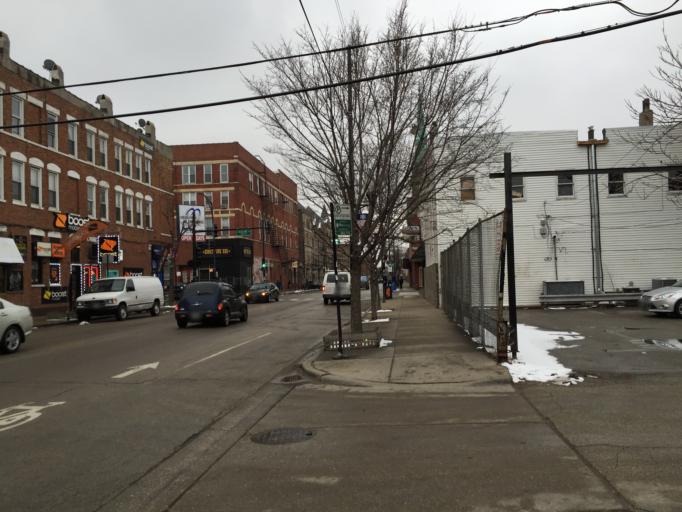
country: US
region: Illinois
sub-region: Cook County
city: Chicago
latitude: 41.8580
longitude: -87.6558
